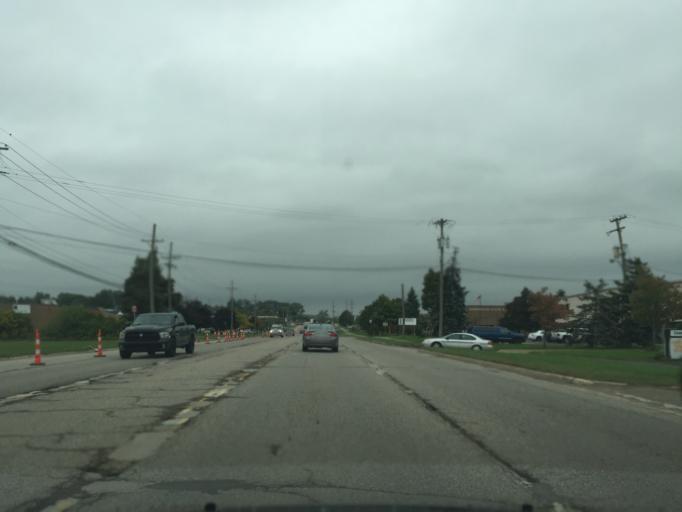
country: US
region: Michigan
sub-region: Oakland County
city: Auburn Hills
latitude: 42.6741
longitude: -83.2459
